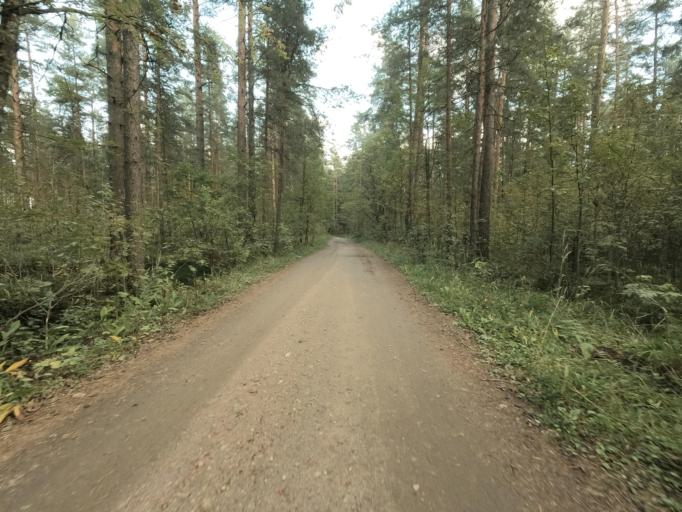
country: RU
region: Leningrad
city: Imeni Sverdlova
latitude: 59.8384
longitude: 30.7124
